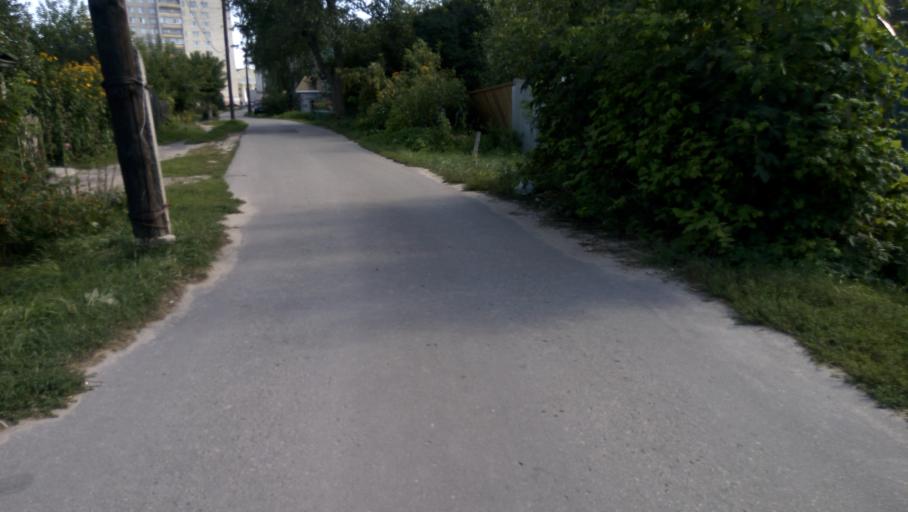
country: RU
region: Nizjnij Novgorod
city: Bor
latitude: 56.3583
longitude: 44.0599
